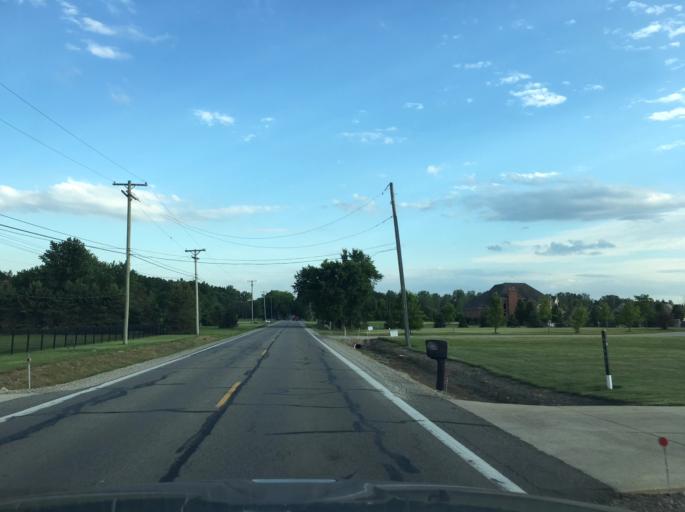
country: US
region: Michigan
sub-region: Macomb County
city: Romeo
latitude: 42.7576
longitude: -82.9610
